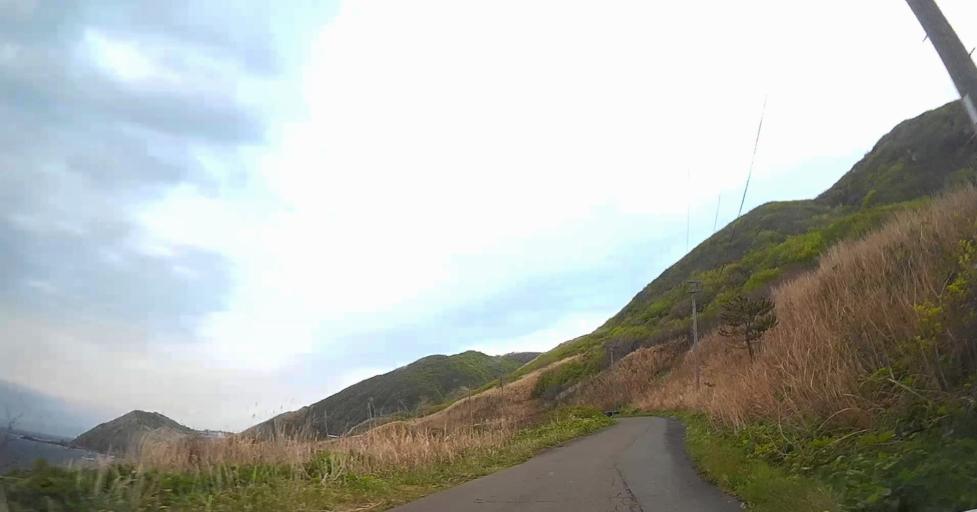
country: JP
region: Aomori
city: Shimokizukuri
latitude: 41.2434
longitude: 140.3424
